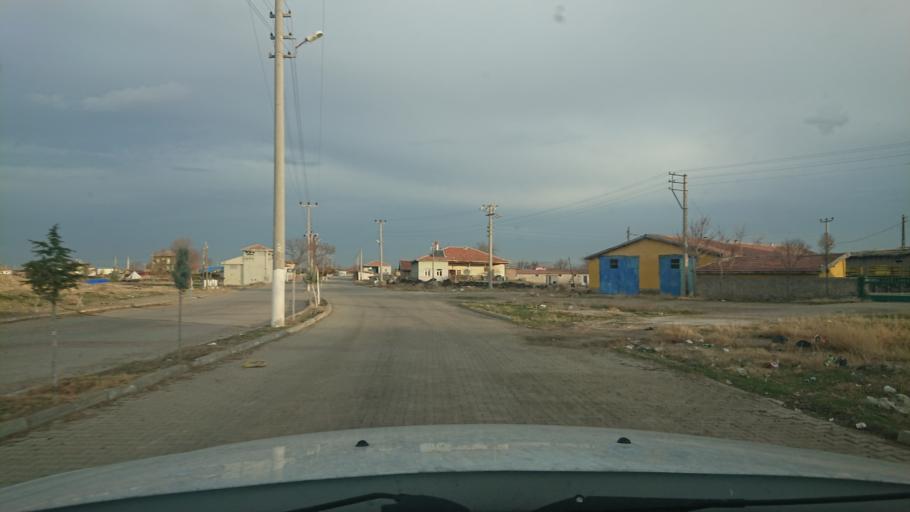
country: TR
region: Aksaray
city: Yesilova
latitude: 38.4123
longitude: 33.8388
